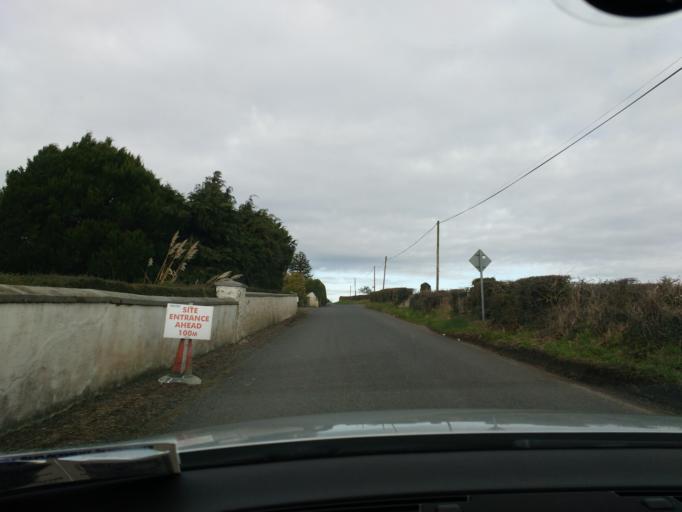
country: IE
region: Leinster
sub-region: Laois
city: Rathdowney
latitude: 52.6813
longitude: -7.6097
